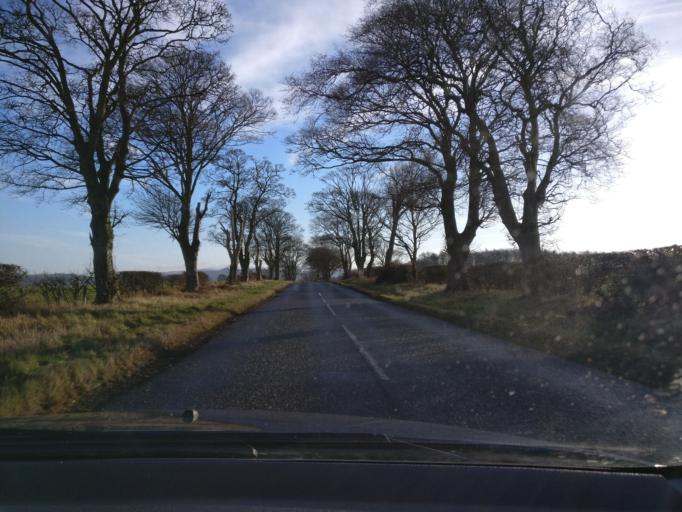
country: GB
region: Scotland
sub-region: The Scottish Borders
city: Kelso
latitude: 55.5284
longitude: -2.4278
